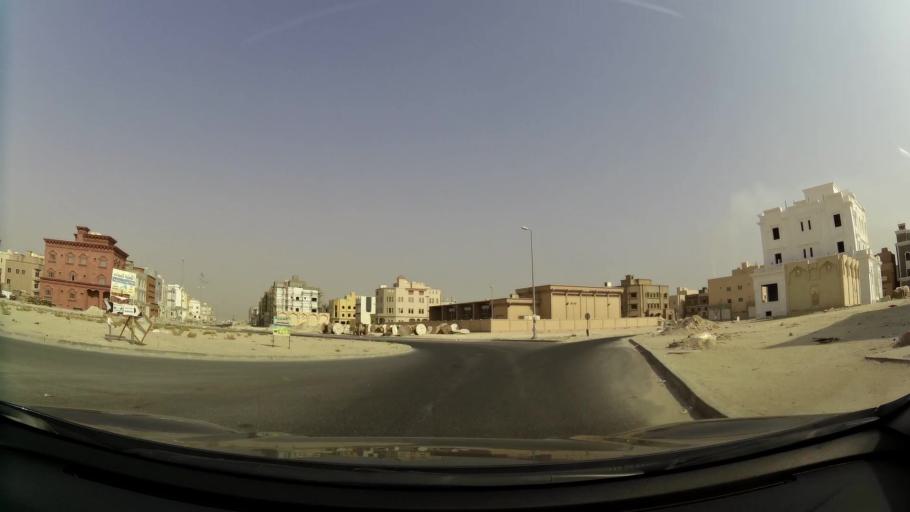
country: KW
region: Muhafazat al Jahra'
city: Al Jahra'
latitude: 29.3535
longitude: 47.7705
